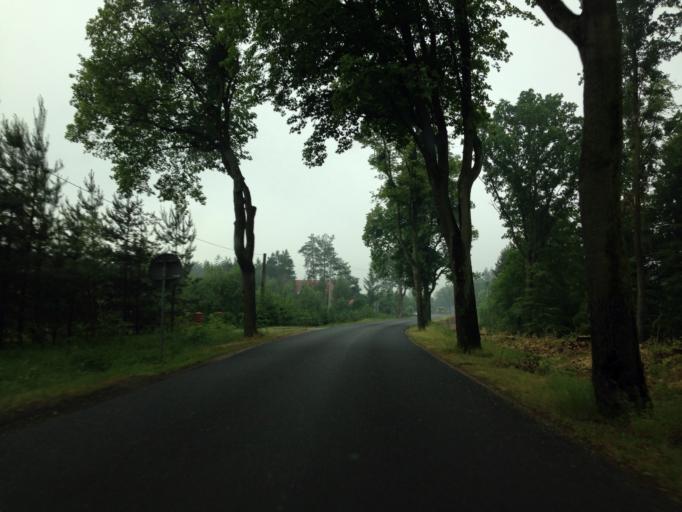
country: PL
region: Kujawsko-Pomorskie
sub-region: Powiat brodnicki
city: Brodnica
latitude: 53.2879
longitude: 19.3884
